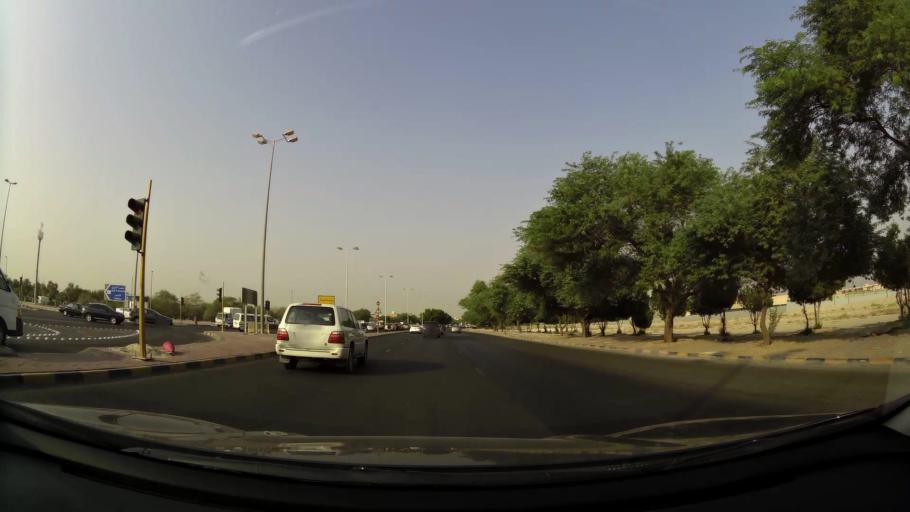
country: KW
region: Al Asimah
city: Ar Rabiyah
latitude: 29.3073
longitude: 47.9049
